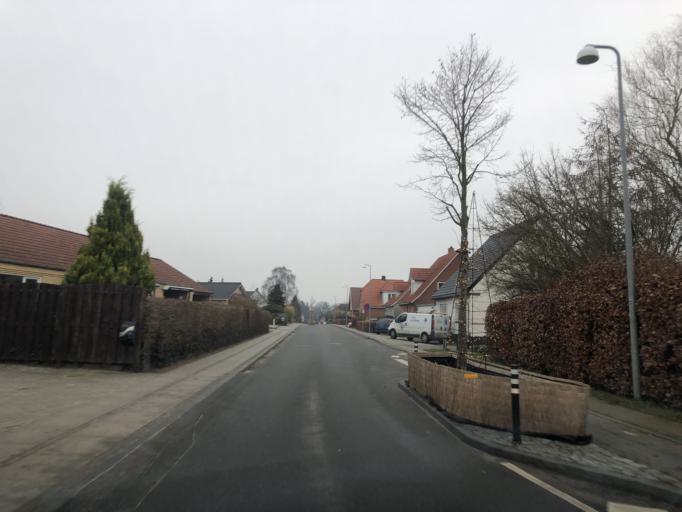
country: DK
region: South Denmark
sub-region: Faaborg-Midtfyn Kommune
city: Arslev
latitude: 55.3060
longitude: 10.4807
